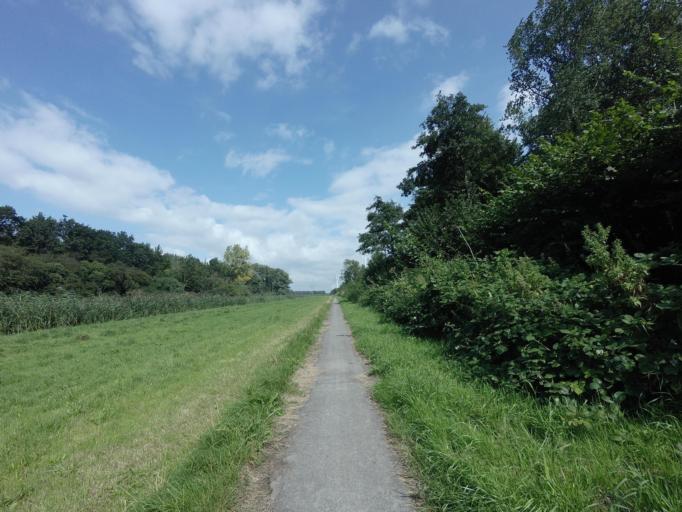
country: NL
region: Flevoland
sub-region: Gemeente Lelystad
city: Lelystad
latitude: 52.5519
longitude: 5.5355
